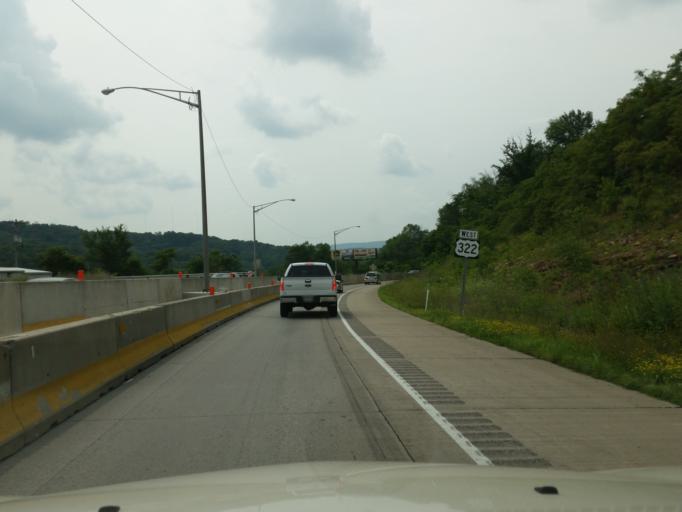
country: US
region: Pennsylvania
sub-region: Mifflin County
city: Lewistown
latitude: 40.5790
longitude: -77.5500
